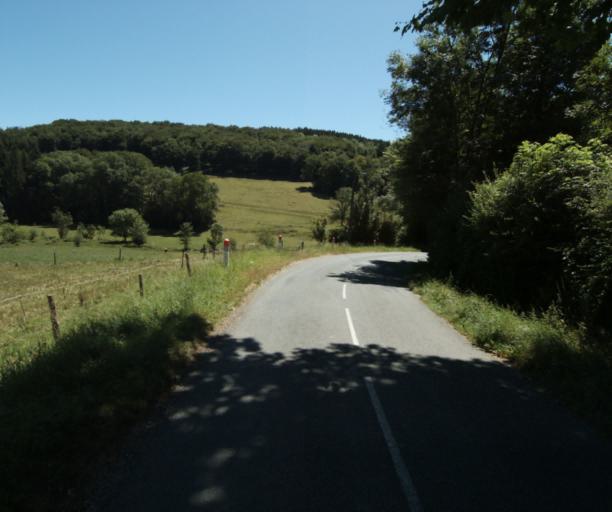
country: FR
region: Midi-Pyrenees
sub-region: Departement du Tarn
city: Dourgne
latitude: 43.4271
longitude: 2.1706
